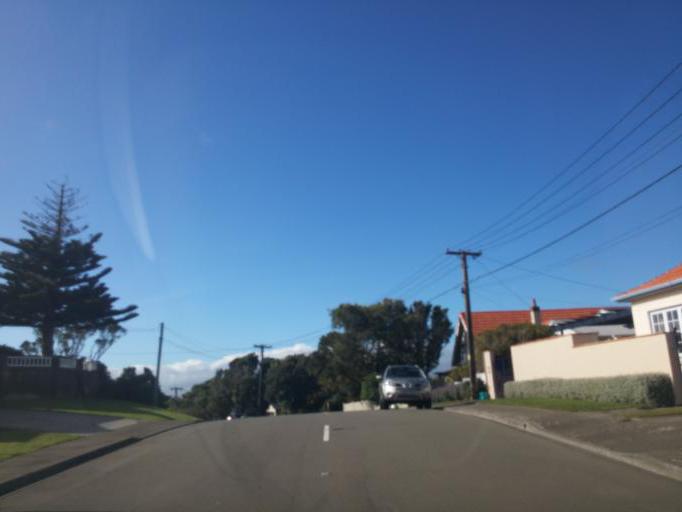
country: NZ
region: Wellington
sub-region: Wellington City
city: Kelburn
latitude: -41.2910
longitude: 174.7480
